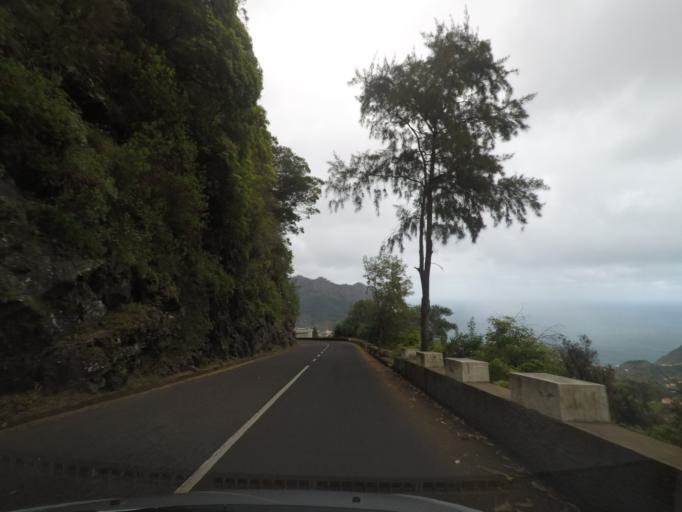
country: PT
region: Madeira
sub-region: Santana
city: Santana
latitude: 32.7504
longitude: -16.8361
